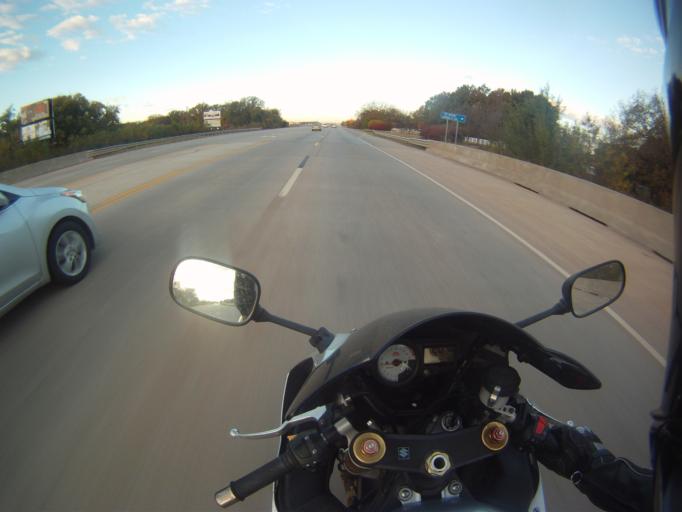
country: US
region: Oklahoma
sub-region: Payne County
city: Stillwater
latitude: 36.1160
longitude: -97.0992
